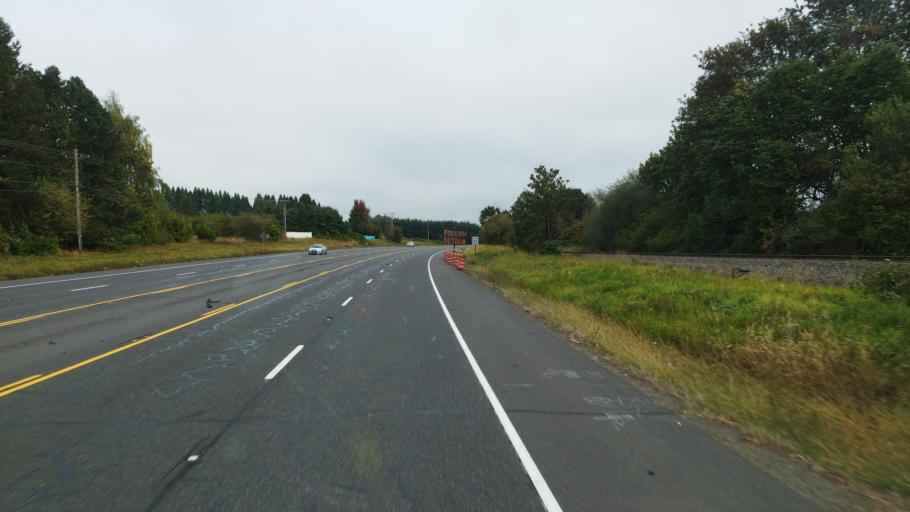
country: US
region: Oregon
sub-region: Columbia County
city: Warren
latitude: 45.7985
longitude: -122.8652
